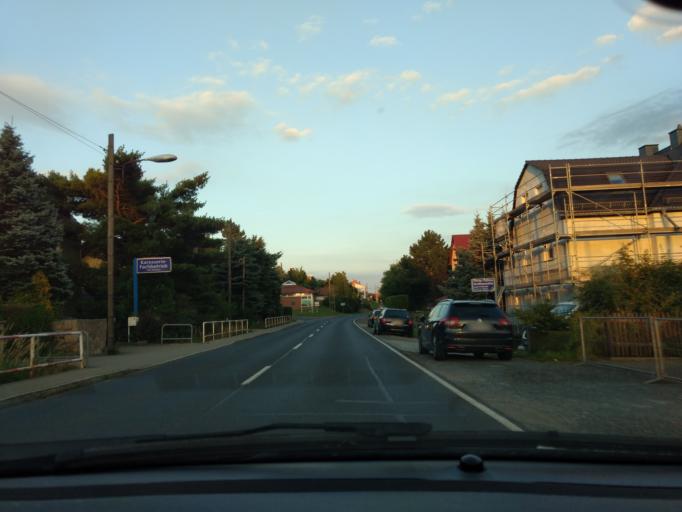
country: DE
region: Saxony
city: Radebeul
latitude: 51.1198
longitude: 13.6917
